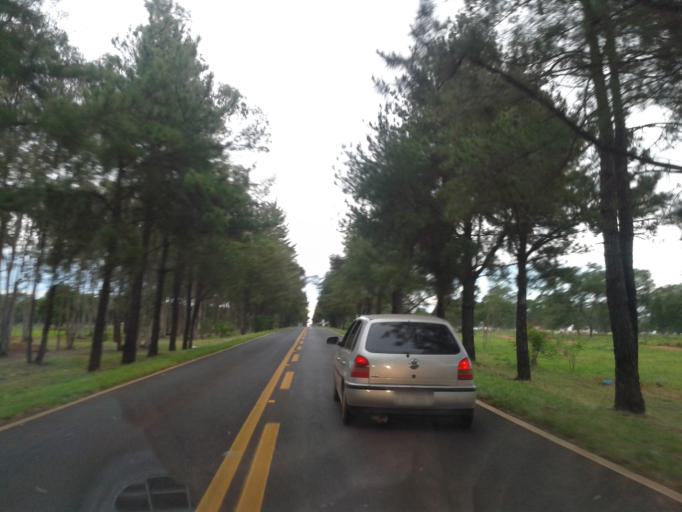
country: BR
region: Minas Gerais
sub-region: Santa Vitoria
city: Santa Vitoria
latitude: -18.8713
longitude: -50.1237
